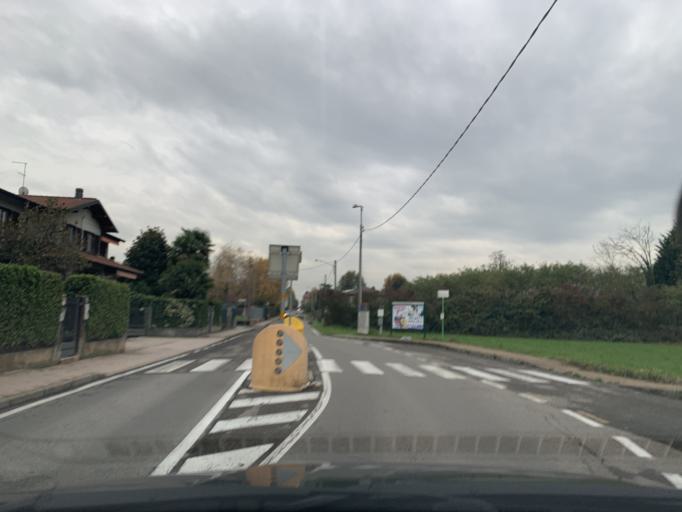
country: IT
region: Lombardy
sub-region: Provincia di Como
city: Bregnano
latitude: 45.7036
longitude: 9.0573
